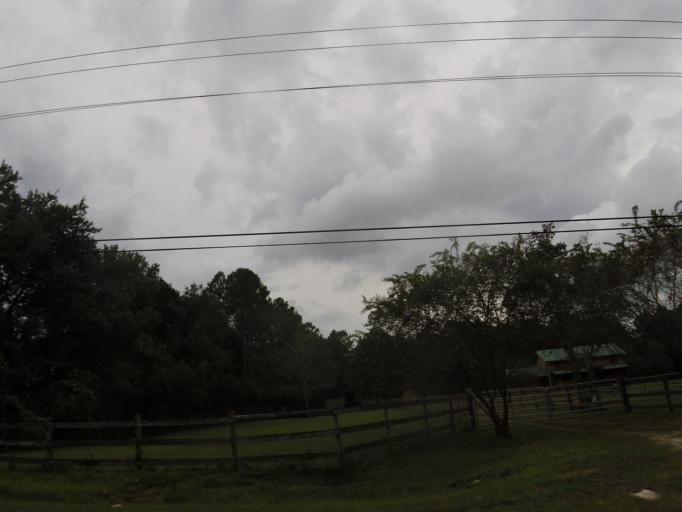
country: US
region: Florida
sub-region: Clay County
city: Middleburg
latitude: 30.1033
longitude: -81.9491
